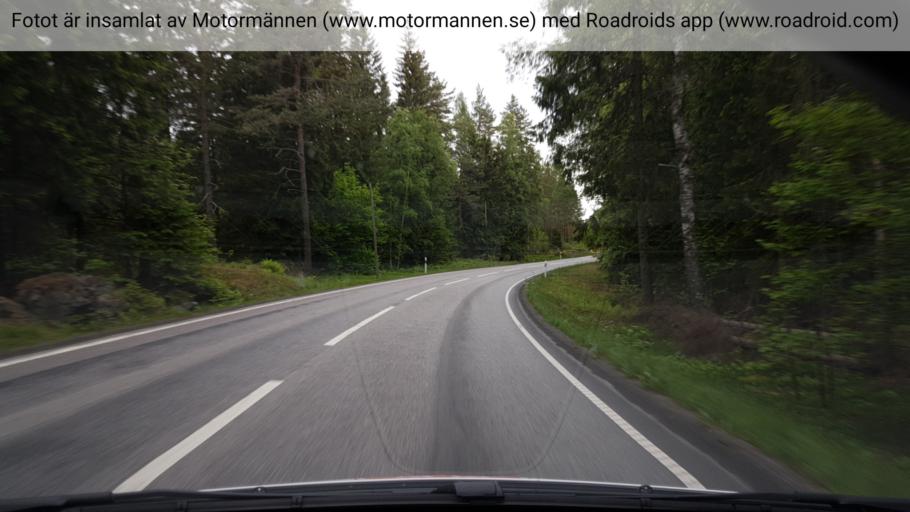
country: SE
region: OErebro
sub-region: Hallsbergs Kommun
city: Palsboda
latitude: 58.8181
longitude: 15.4127
